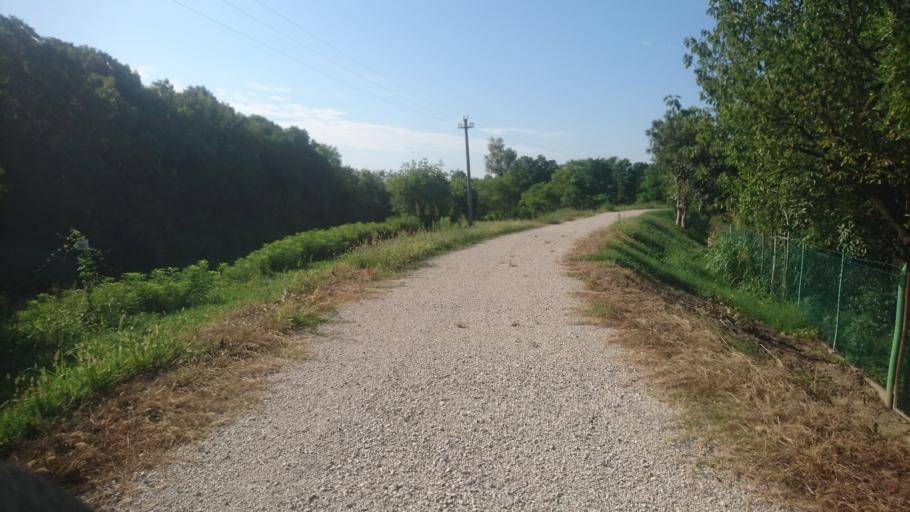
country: IT
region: Veneto
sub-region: Provincia di Padova
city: Sarmeola
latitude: 45.4321
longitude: 11.8281
